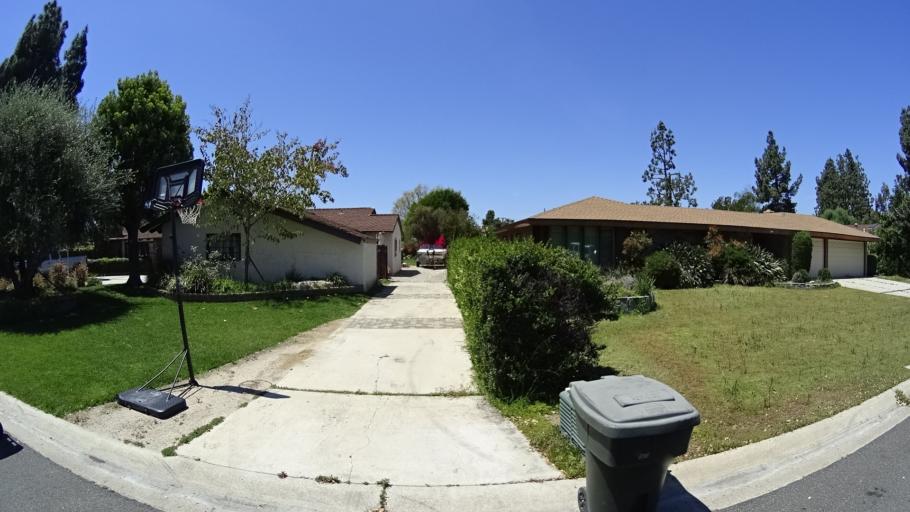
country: US
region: California
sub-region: Orange County
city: Villa Park
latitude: 33.8085
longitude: -117.8118
